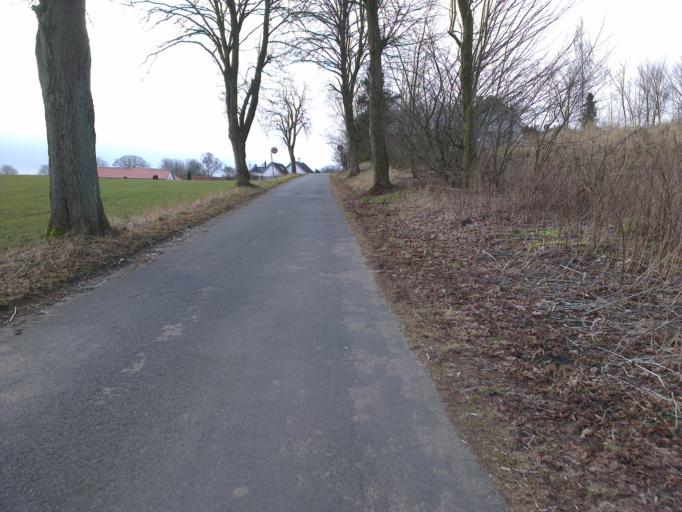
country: DK
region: Capital Region
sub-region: Frederikssund Kommune
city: Skibby
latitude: 55.7897
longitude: 11.9620
